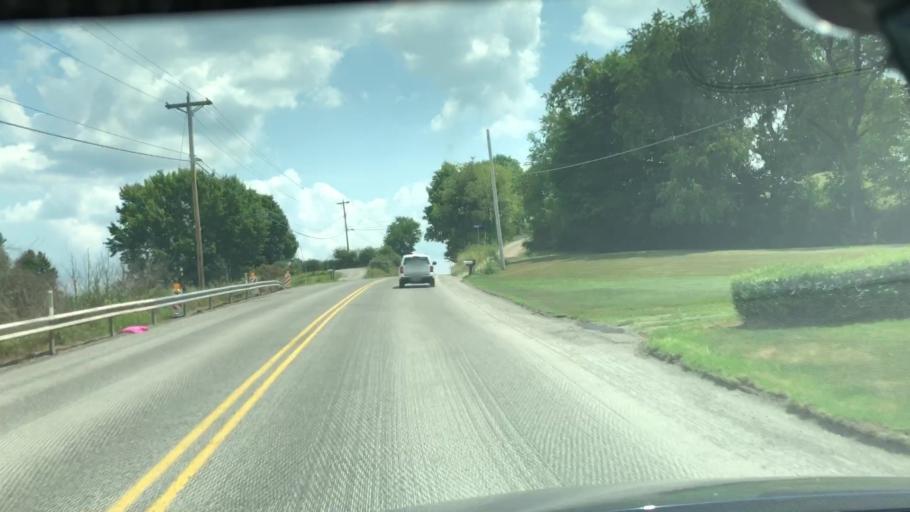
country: US
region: Pennsylvania
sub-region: Butler County
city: Saxonburg
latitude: 40.8066
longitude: -79.8311
